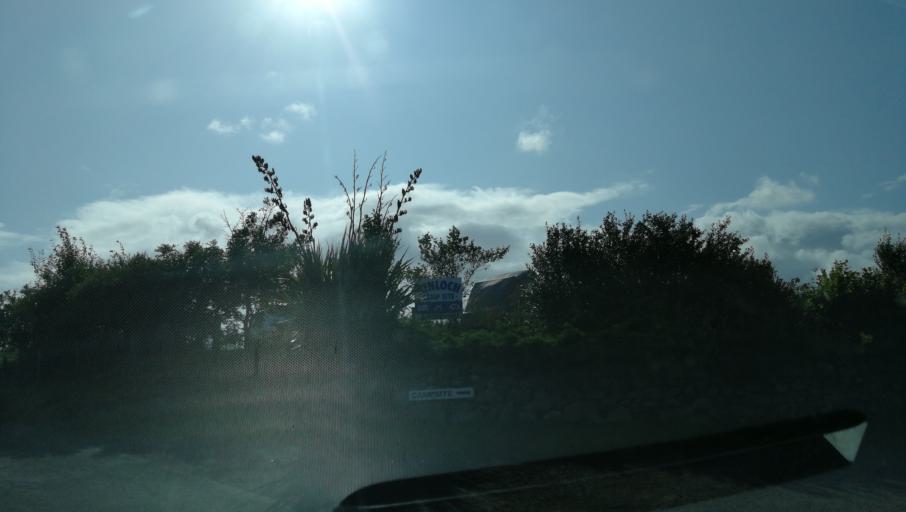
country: GB
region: Scotland
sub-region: Highland
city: Isle of Skye
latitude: 57.4316
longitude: -6.5780
